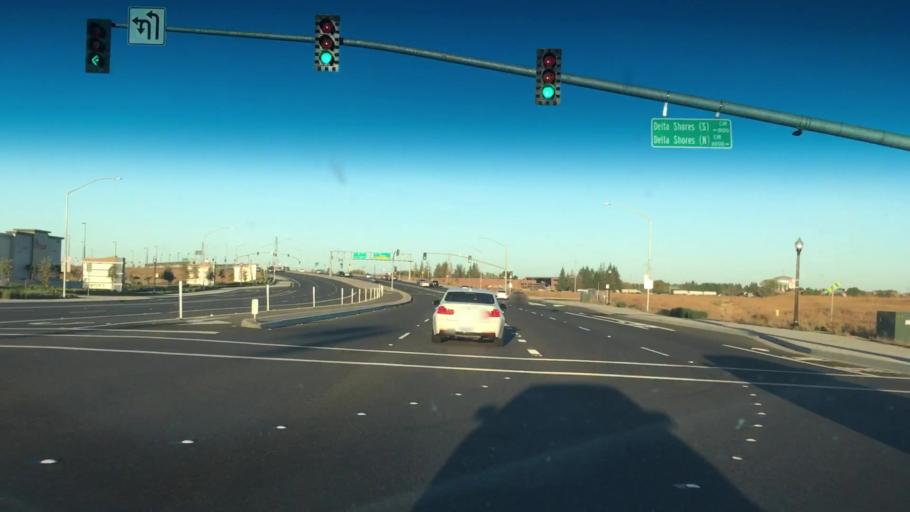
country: US
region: California
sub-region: Sacramento County
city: Parkway
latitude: 38.4666
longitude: -121.4909
